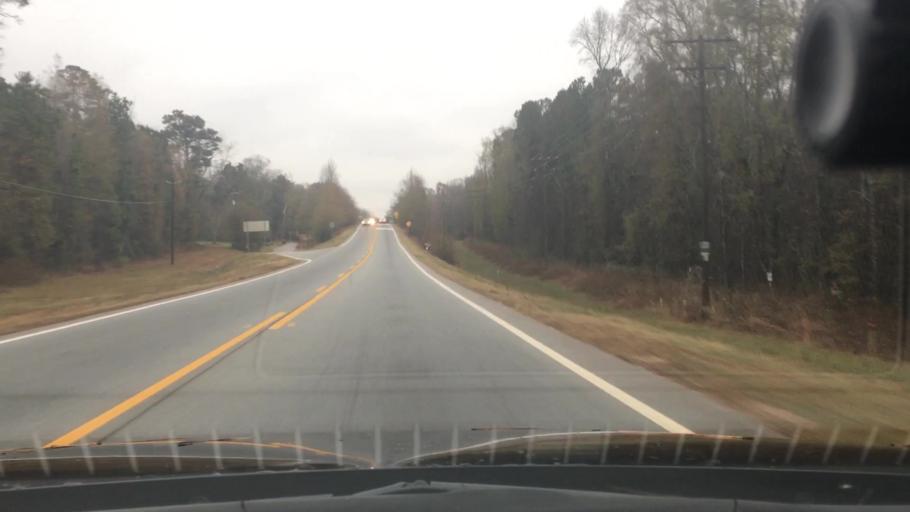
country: US
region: Georgia
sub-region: Fayette County
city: Peachtree City
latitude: 33.3338
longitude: -84.6466
